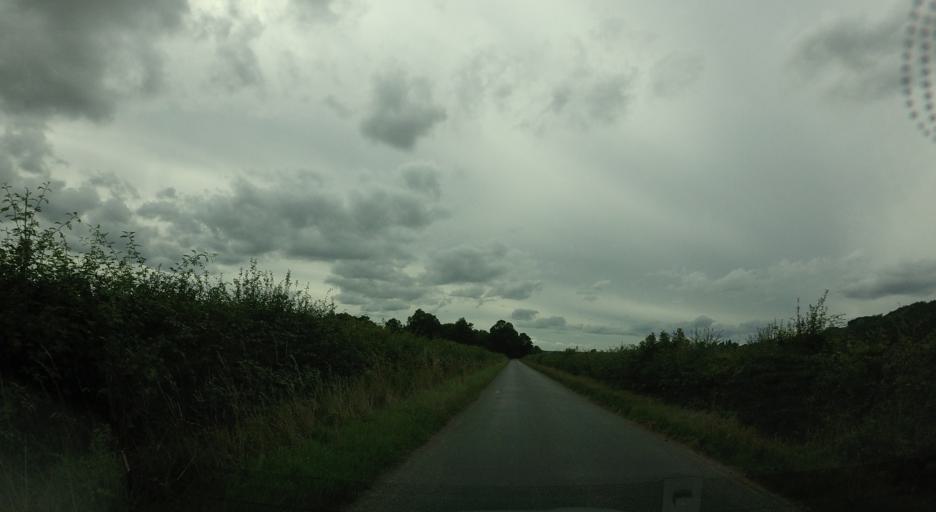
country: GB
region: Scotland
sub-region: Perth and Kinross
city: Bridge of Earn
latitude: 56.3542
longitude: -3.3834
